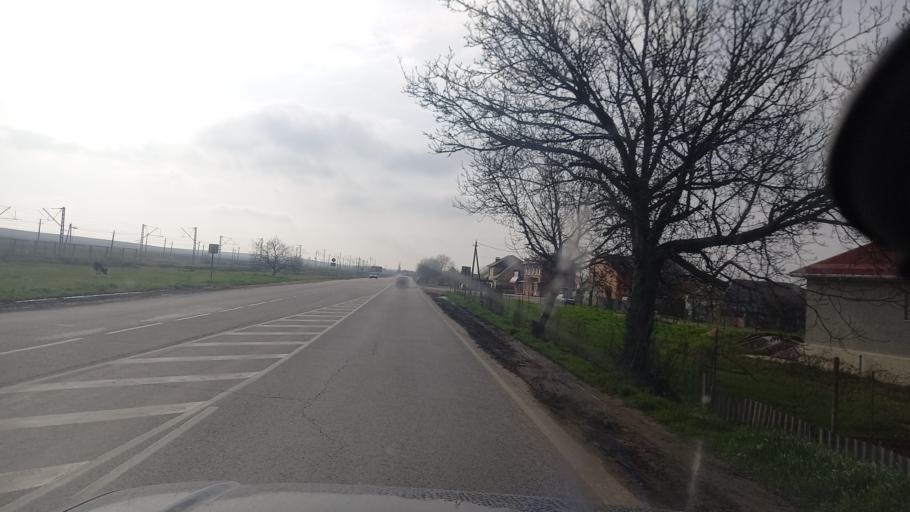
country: RU
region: Krasnodarskiy
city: Varenikovskaya
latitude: 45.1123
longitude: 37.6317
